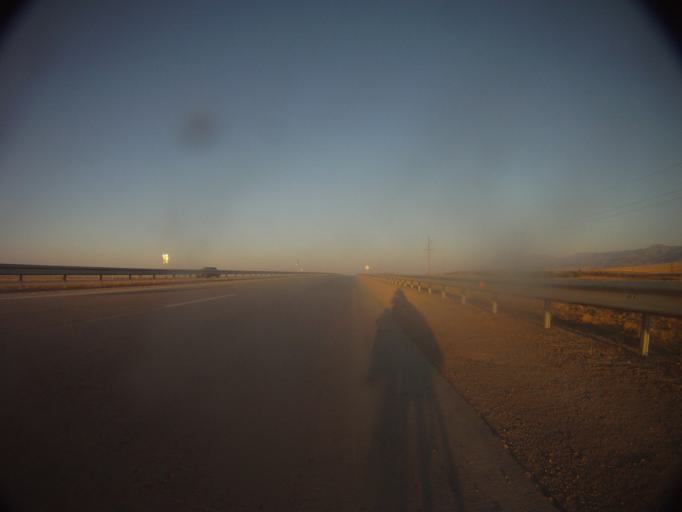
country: KZ
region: Zhambyl
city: Sarykemer
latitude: 43.0087
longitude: 71.6541
